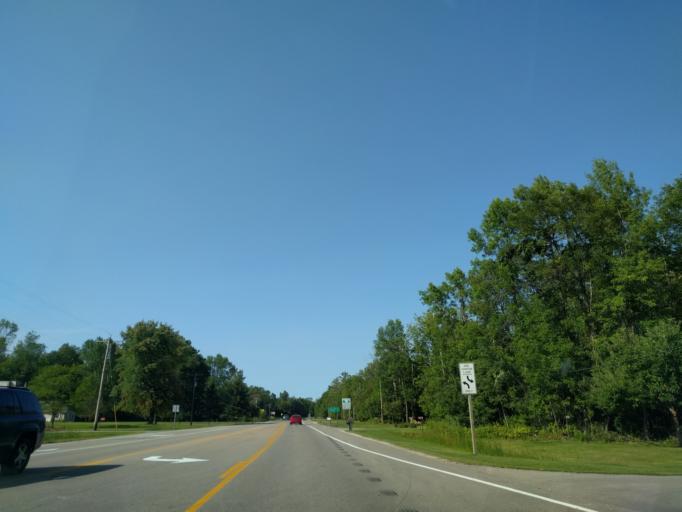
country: US
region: Michigan
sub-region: Menominee County
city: Menominee
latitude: 45.1439
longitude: -87.6031
